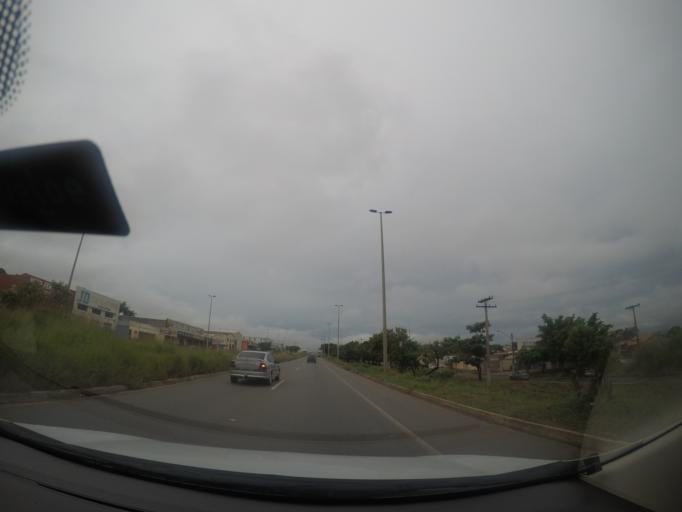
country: BR
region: Goias
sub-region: Aparecida De Goiania
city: Aparecida de Goiania
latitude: -16.7576
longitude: -49.3414
